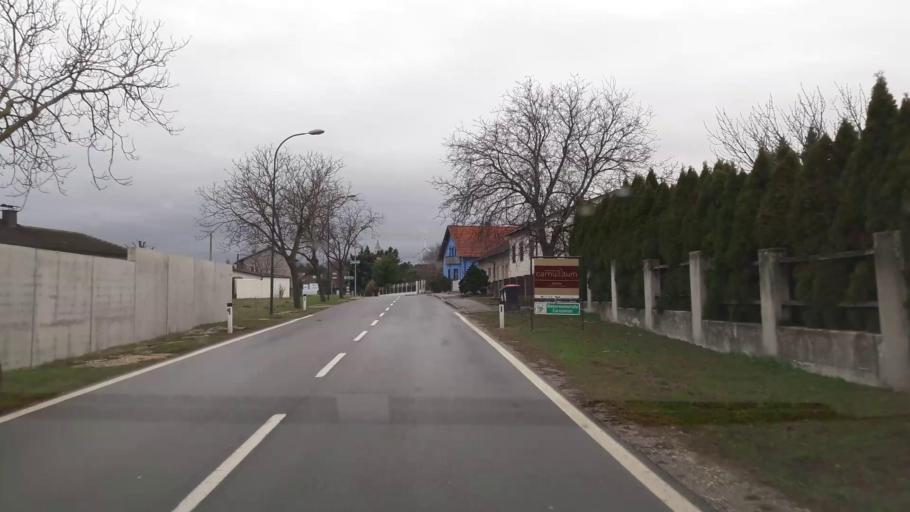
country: AT
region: Lower Austria
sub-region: Politischer Bezirk Bruck an der Leitha
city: Scharndorf
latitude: 48.0709
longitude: 16.7916
